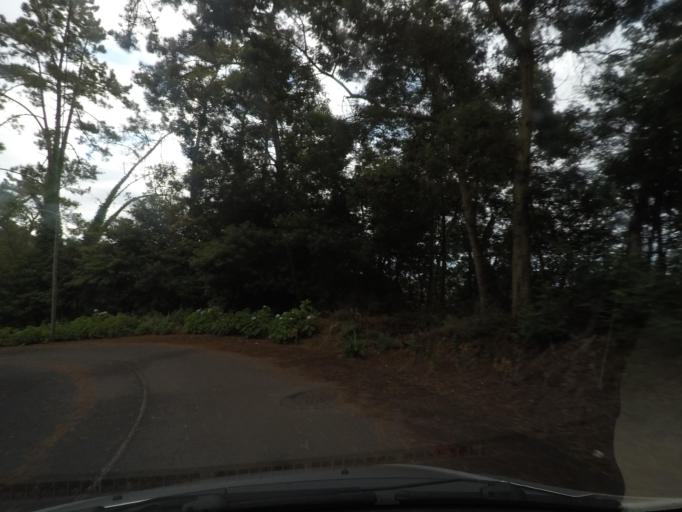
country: PT
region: Madeira
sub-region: Santana
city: Santana
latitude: 32.7887
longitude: -16.8786
